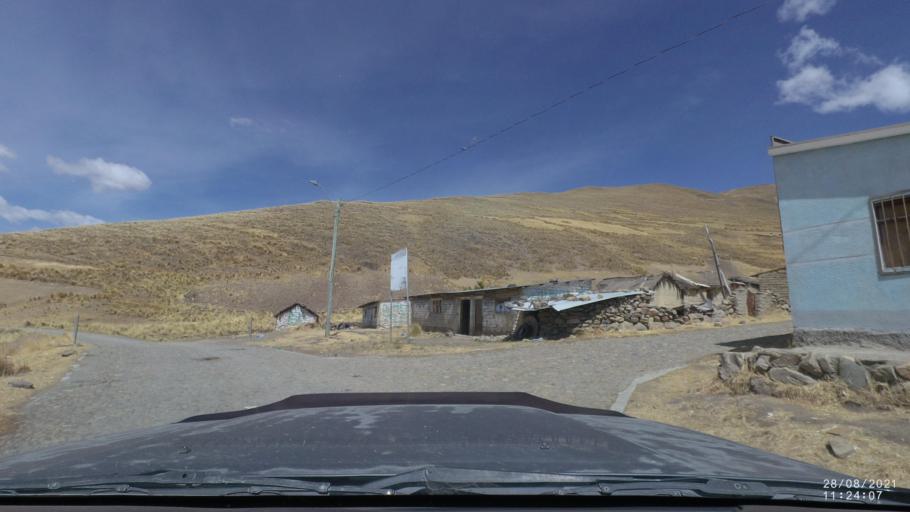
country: BO
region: Cochabamba
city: Sipe Sipe
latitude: -17.1654
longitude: -66.3520
